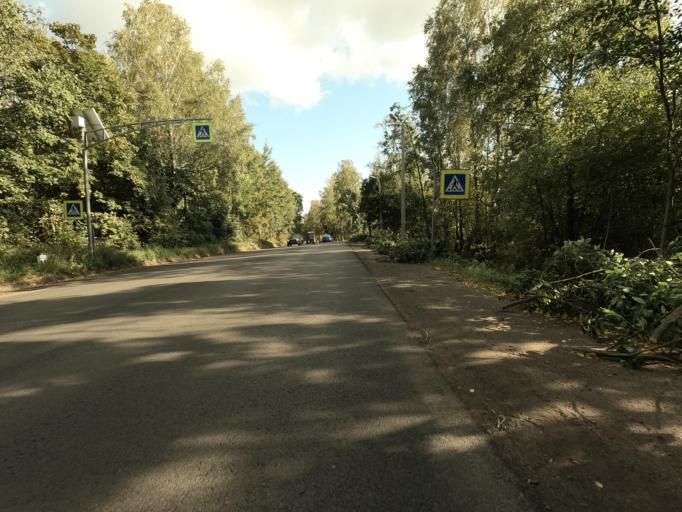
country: RU
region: Leningrad
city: Koltushi
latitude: 59.9407
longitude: 30.6569
